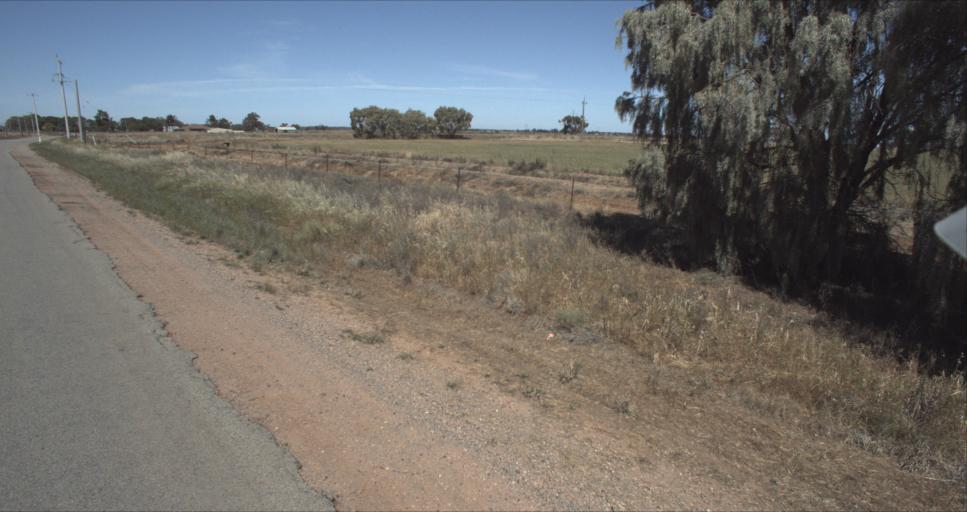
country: AU
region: New South Wales
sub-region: Leeton
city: Leeton
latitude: -34.5659
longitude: 146.3118
